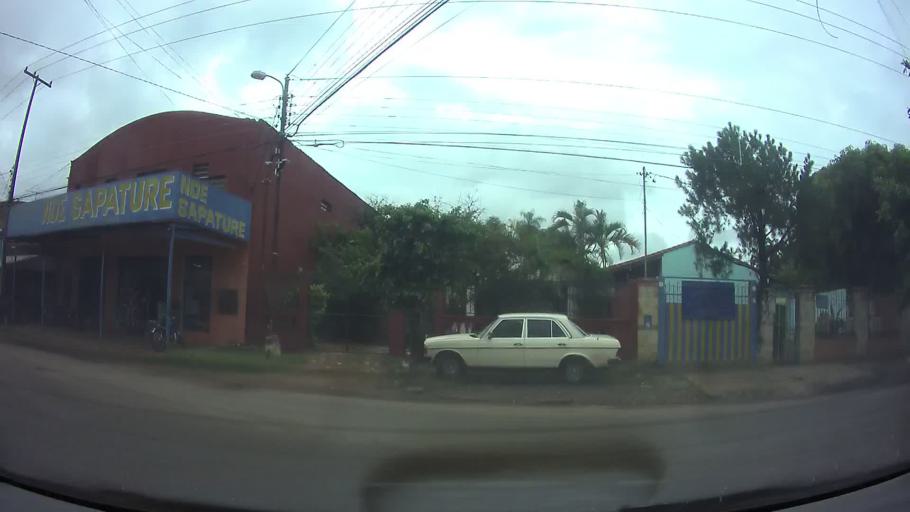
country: PY
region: Central
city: San Lorenzo
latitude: -25.2724
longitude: -57.4832
